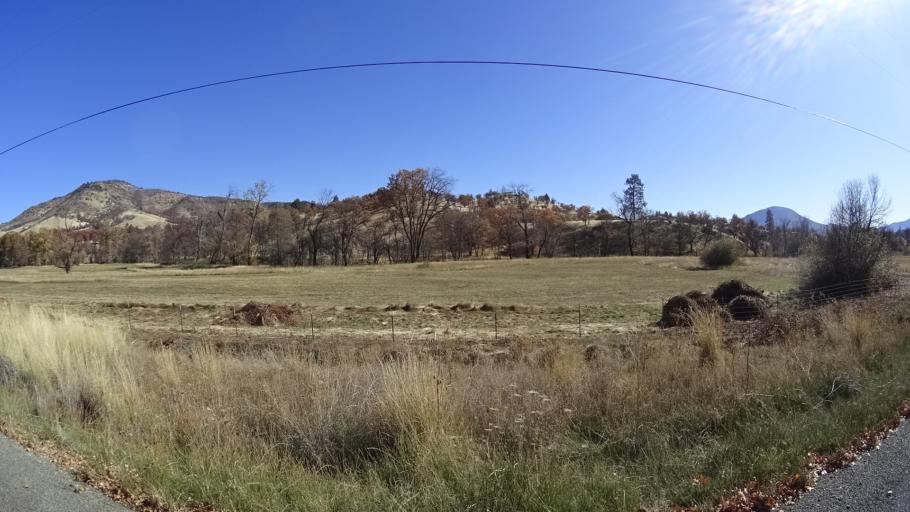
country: US
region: California
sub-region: Siskiyou County
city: Yreka
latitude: 41.9388
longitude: -122.5917
